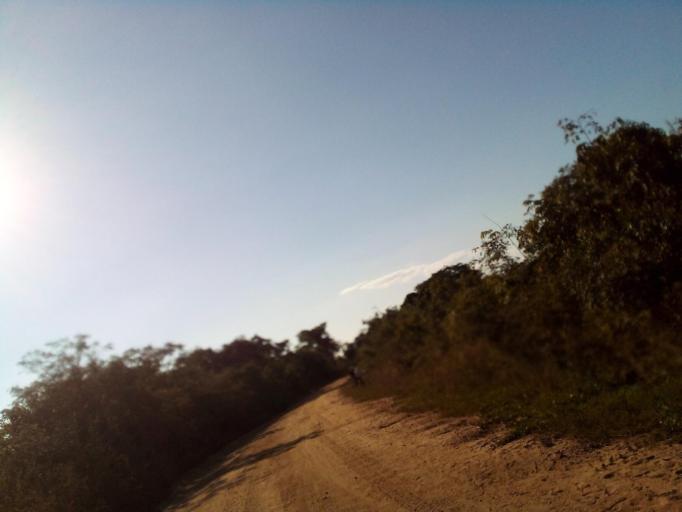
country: MZ
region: Zambezia
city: Quelimane
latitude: -17.4802
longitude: 36.5427
